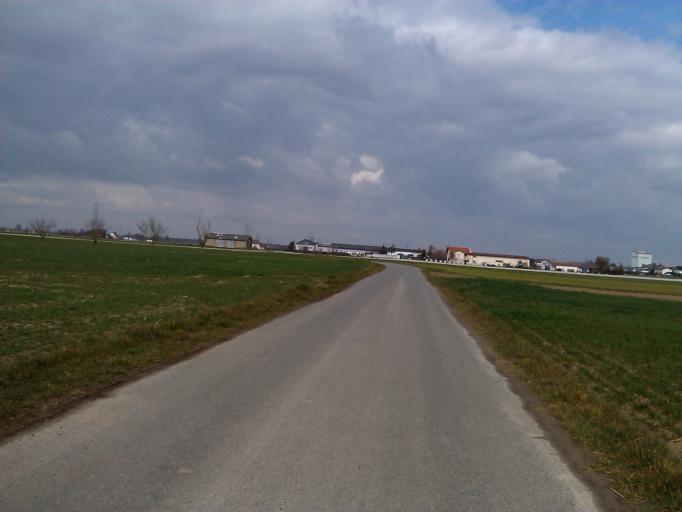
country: DE
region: Hesse
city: Pfungstadt
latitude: 49.7909
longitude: 8.5968
